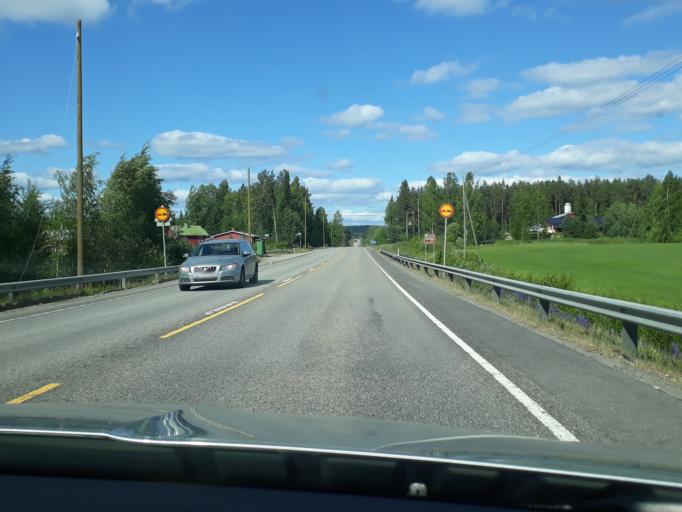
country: FI
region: Central Finland
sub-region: AEaenekoski
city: AEaenekoski
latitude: 62.6542
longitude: 25.7226
